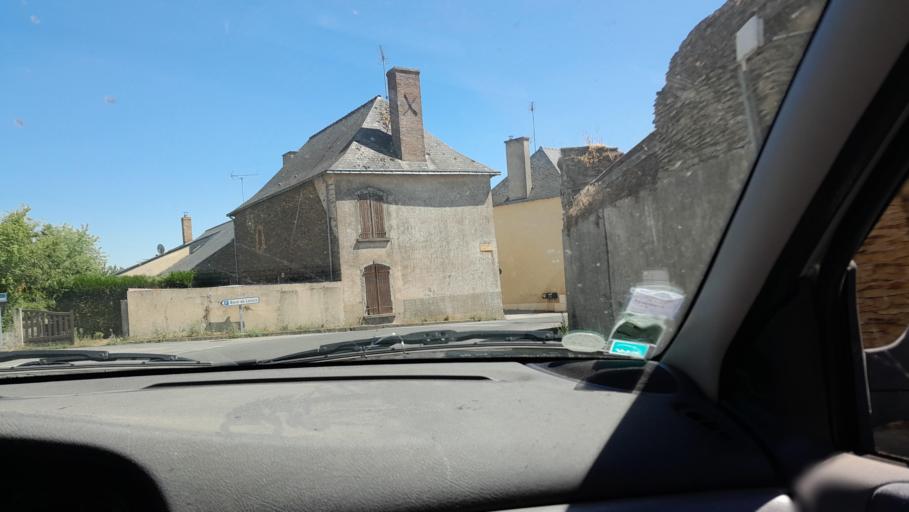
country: FR
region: Pays de la Loire
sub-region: Departement de Maine-et-Loire
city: Pouance
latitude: 47.7522
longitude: -1.1789
